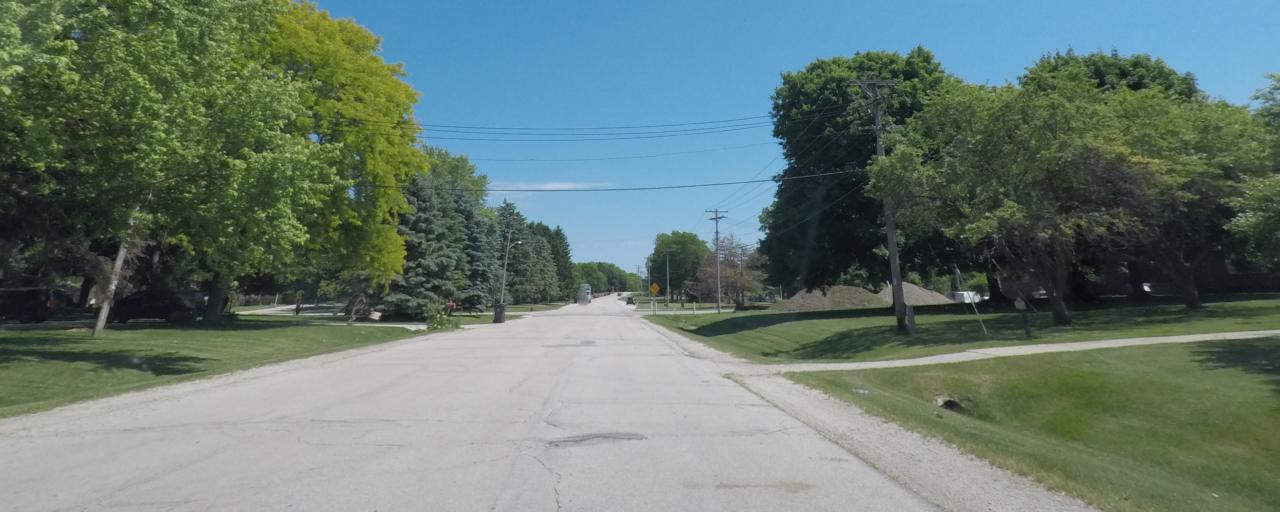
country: US
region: Wisconsin
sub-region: Milwaukee County
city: Hales Corners
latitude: 42.9424
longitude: -88.0638
